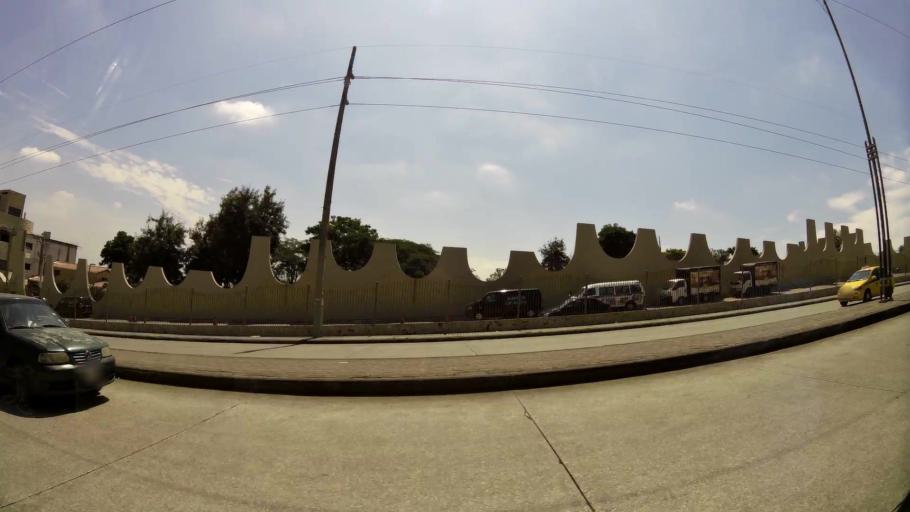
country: EC
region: Guayas
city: Guayaquil
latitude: -2.1335
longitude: -79.9238
